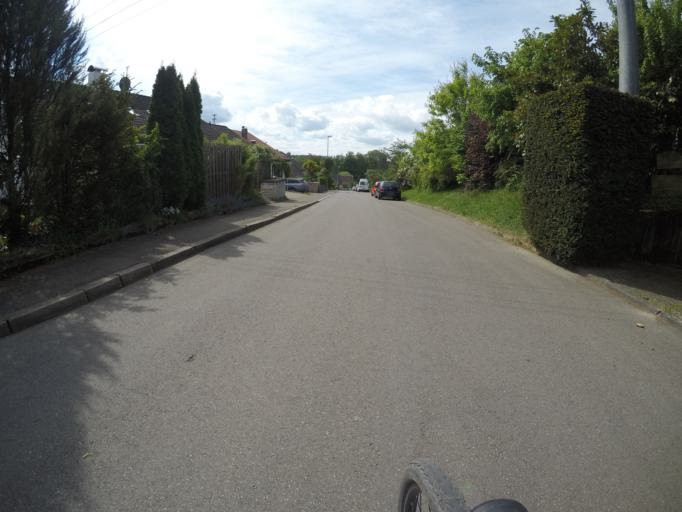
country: DE
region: Baden-Wuerttemberg
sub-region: Tuebingen Region
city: Tuebingen
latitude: 48.5420
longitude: 9.0066
